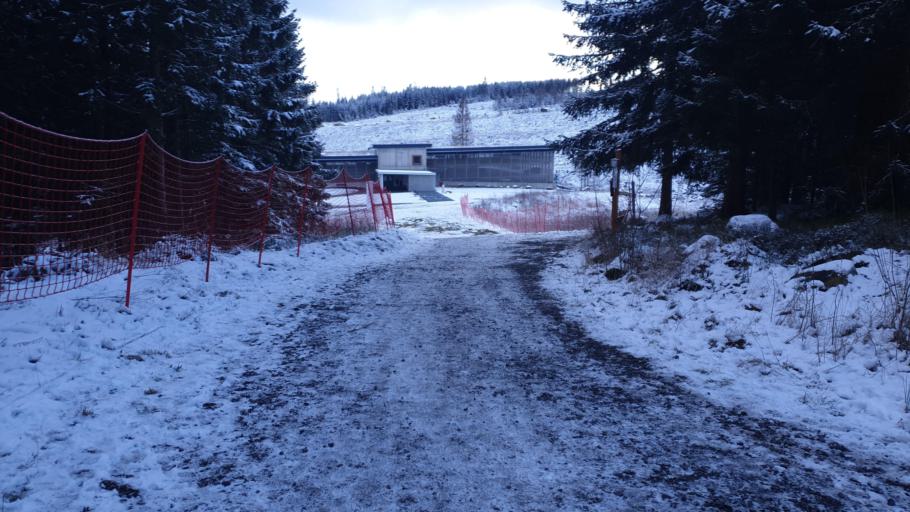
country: DE
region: Lower Saxony
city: Braunlage
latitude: 51.7667
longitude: 10.6510
